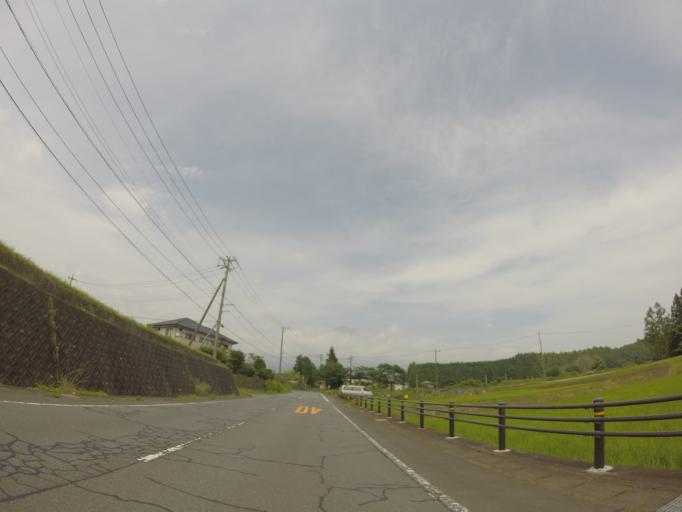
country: JP
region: Shizuoka
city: Fujinomiya
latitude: 35.2990
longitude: 138.5878
